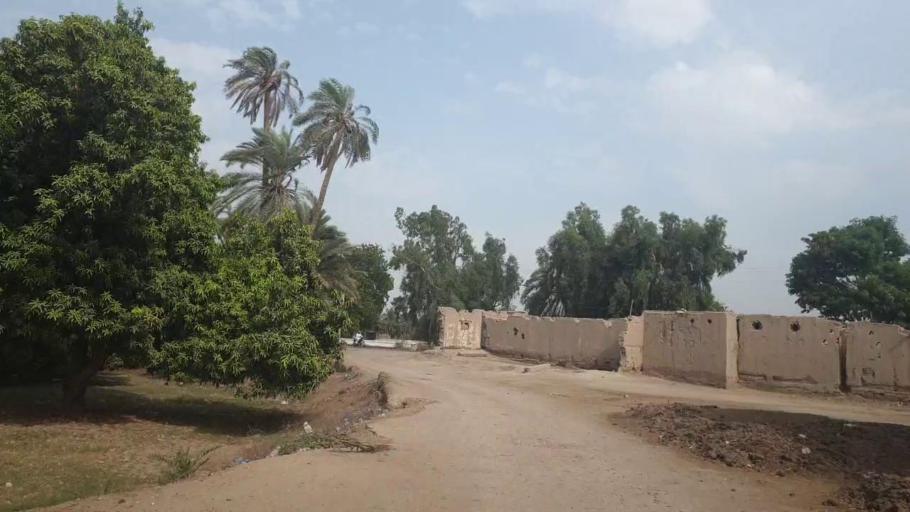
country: PK
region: Sindh
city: Sukkur
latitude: 27.6423
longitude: 68.7995
